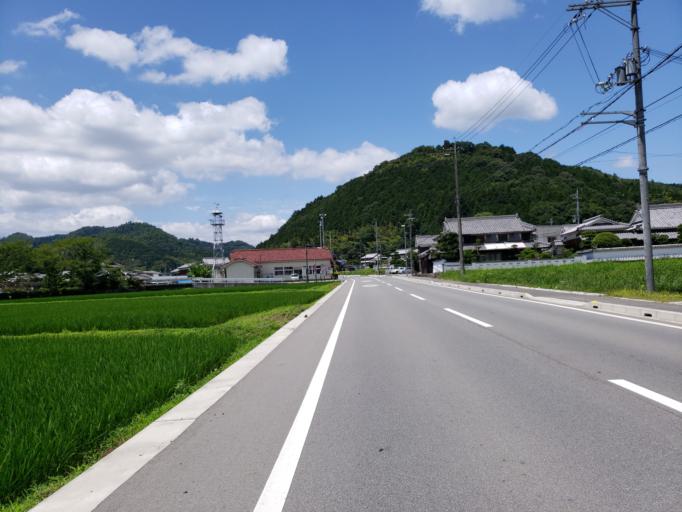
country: JP
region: Hyogo
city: Himeji
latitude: 34.9413
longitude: 134.7191
